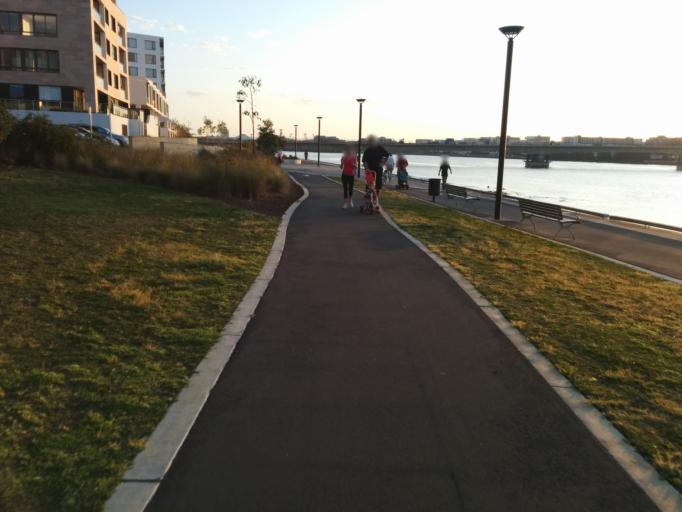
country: AU
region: New South Wales
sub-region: Canada Bay
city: Rhodes
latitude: -33.8265
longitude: 151.0844
